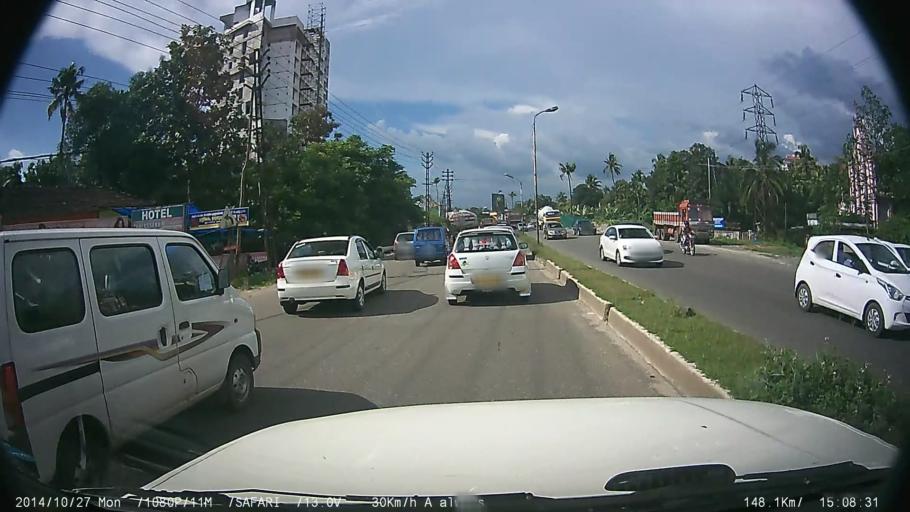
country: IN
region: Kerala
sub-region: Ernakulam
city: Aluva
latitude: 10.1155
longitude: 76.3451
